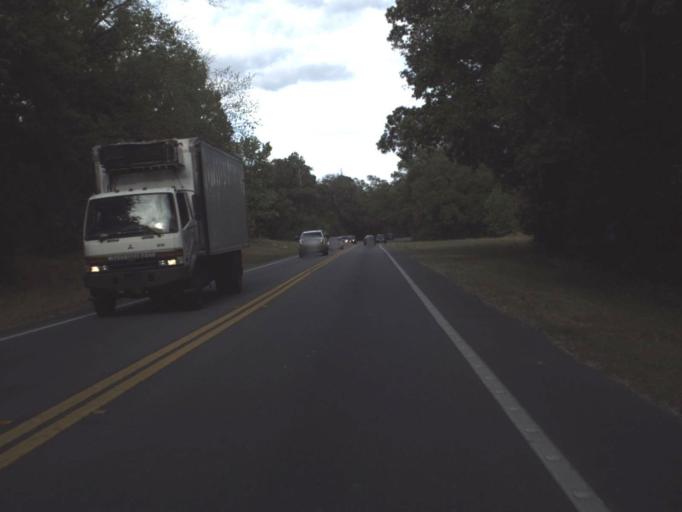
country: US
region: Florida
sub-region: Marion County
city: Ocala
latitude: 29.2194
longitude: -82.0419
